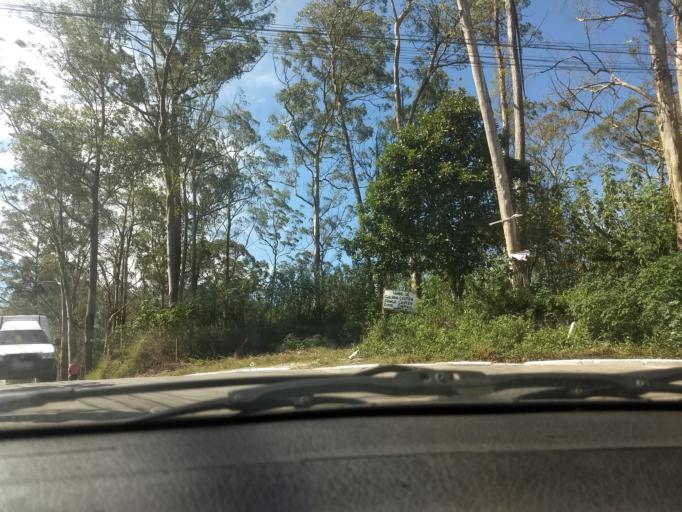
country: BR
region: Sao Paulo
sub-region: Embu-Guacu
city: Embu Guacu
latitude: -23.8269
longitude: -46.7114
